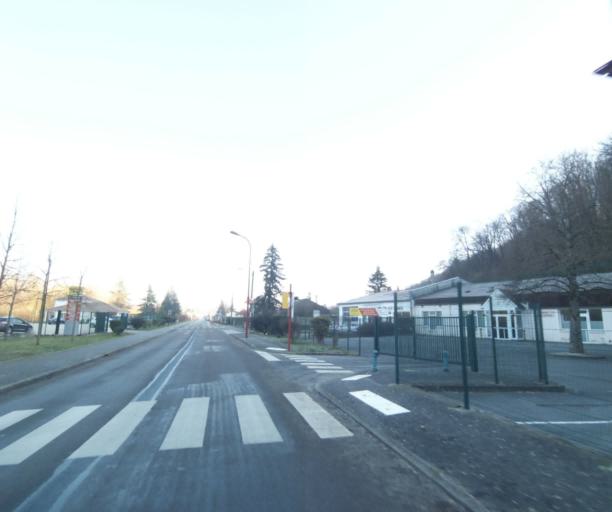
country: FR
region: Champagne-Ardenne
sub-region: Departement de la Haute-Marne
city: Bienville
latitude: 48.5464
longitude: 5.0784
